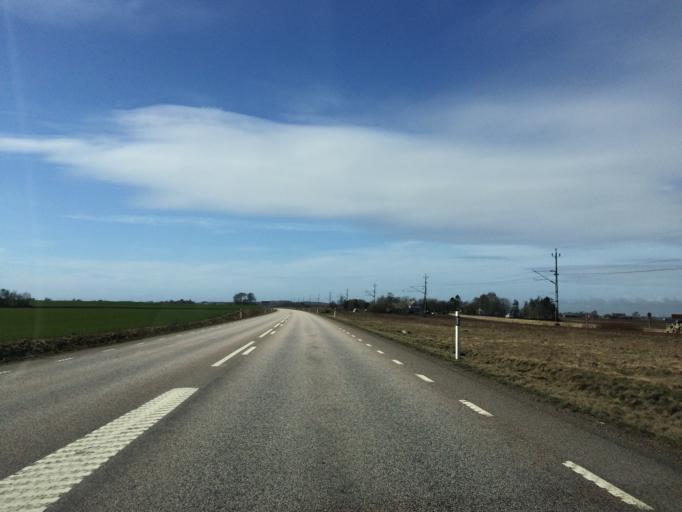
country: SE
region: Halland
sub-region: Laholms Kommun
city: Veinge
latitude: 56.5412
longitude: 13.1458
